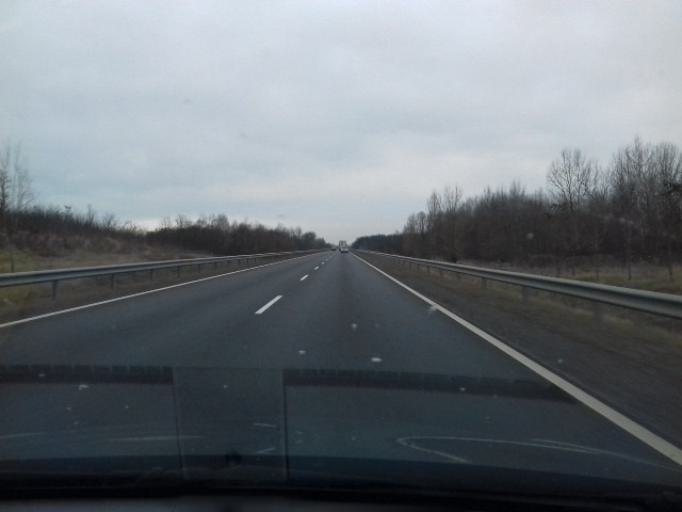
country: HU
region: Szabolcs-Szatmar-Bereg
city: Nagykallo
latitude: 47.9152
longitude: 21.8190
